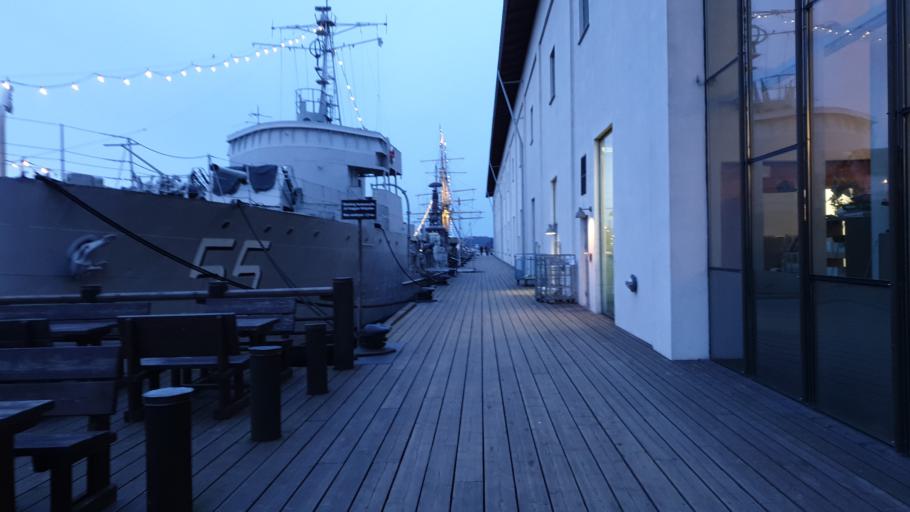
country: SE
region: Blekinge
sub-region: Karlskrona Kommun
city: Karlskrona
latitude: 56.1612
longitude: 15.5990
